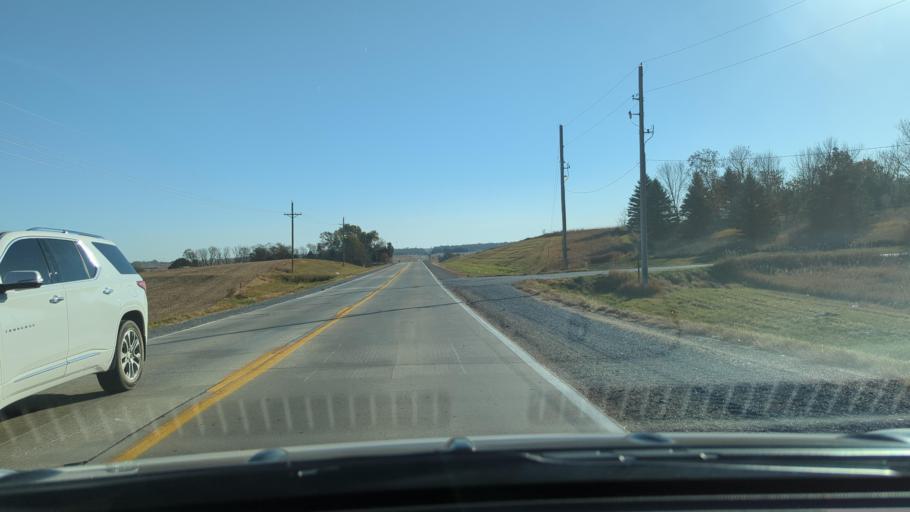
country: US
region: Nebraska
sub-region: Sarpy County
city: Papillion
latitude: 41.0926
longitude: -96.0169
